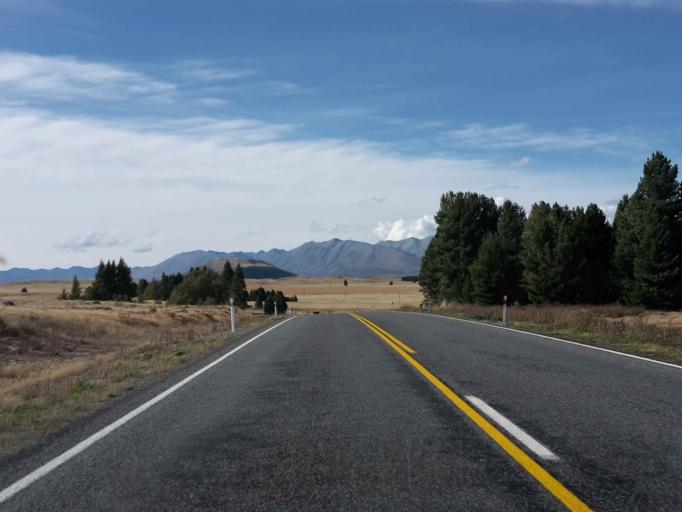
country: NZ
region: Canterbury
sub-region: Timaru District
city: Pleasant Point
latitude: -44.0315
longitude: 170.3922
